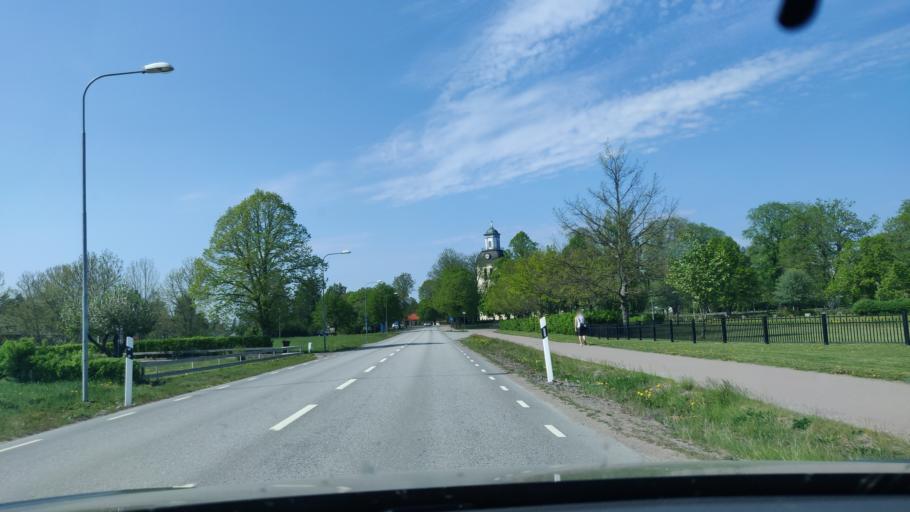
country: SE
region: Uppsala
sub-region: Heby Kommun
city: OEstervala
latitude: 60.1768
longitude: 17.1797
